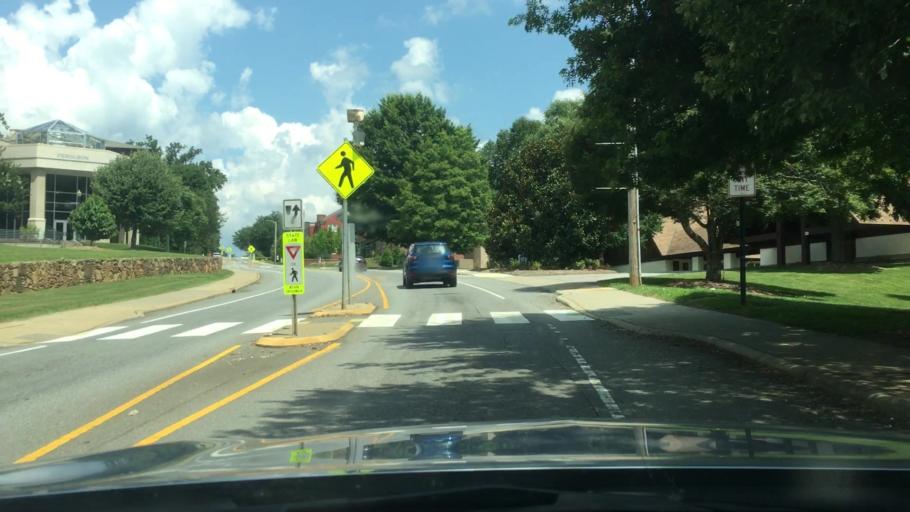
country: US
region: North Carolina
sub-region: Madison County
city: Mars Hill
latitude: 35.8265
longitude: -82.5539
